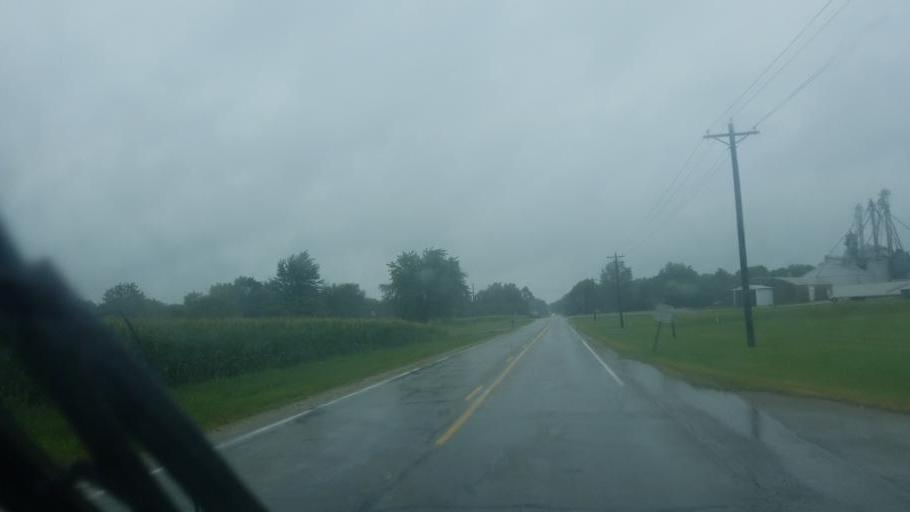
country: US
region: Indiana
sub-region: Huntington County
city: Warren
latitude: 40.6718
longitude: -85.4148
